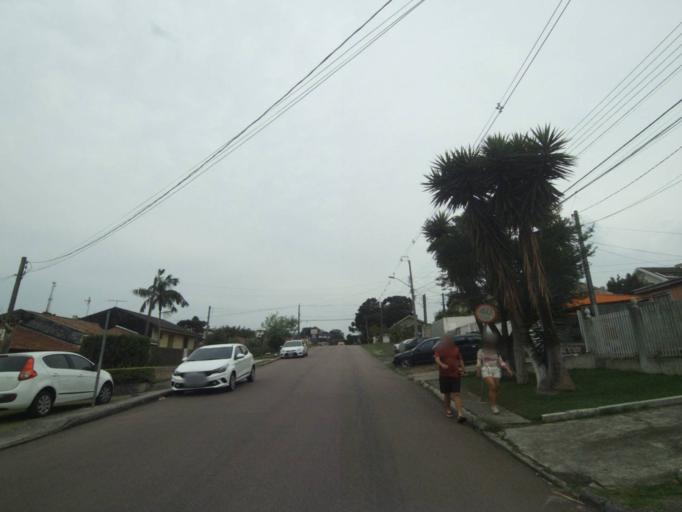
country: BR
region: Parana
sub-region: Pinhais
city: Pinhais
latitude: -25.4190
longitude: -49.2106
